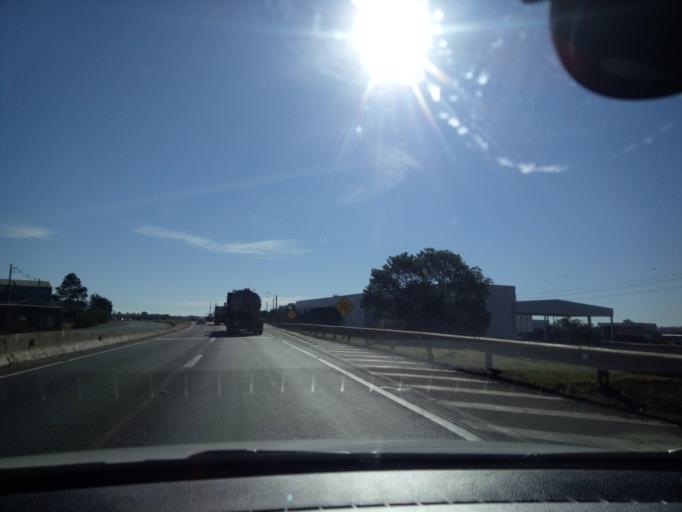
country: BR
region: Rio Grande do Sul
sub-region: Esteio
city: Esteio
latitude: -29.8495
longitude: -51.2677
